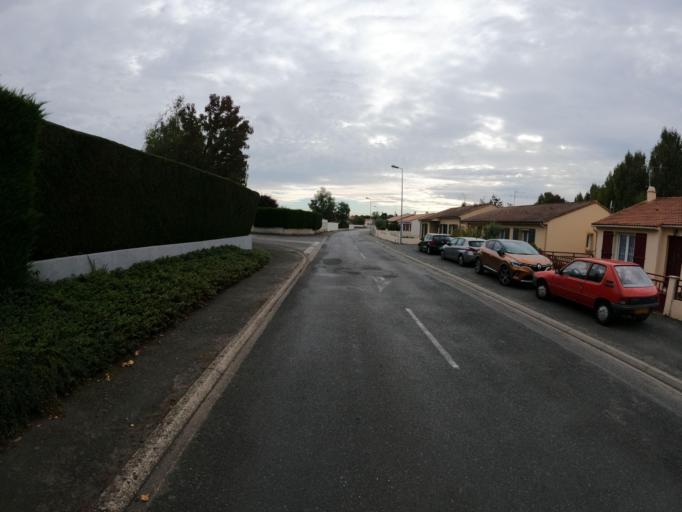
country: FR
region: Pays de la Loire
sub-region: Departement de Maine-et-Loire
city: Saint-Christophe-du-Bois
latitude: 47.0321
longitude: -0.9413
